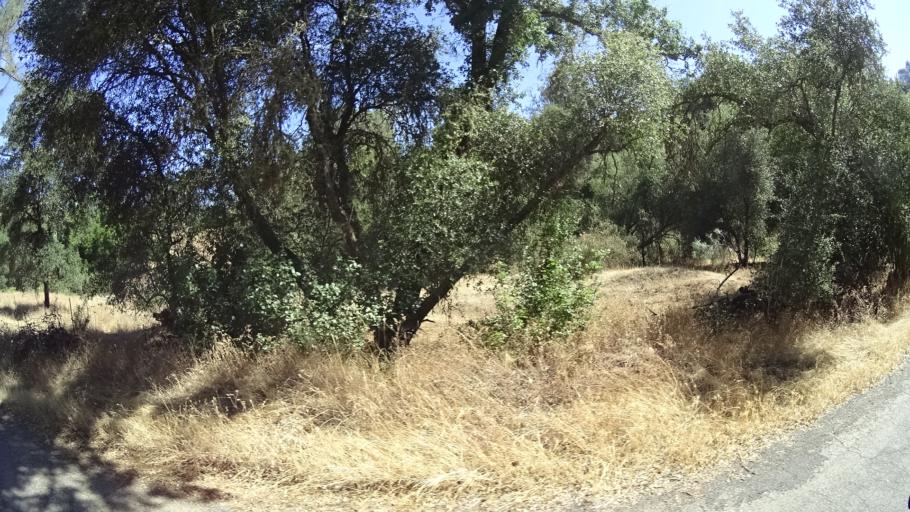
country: US
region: California
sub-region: Calaveras County
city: Angels Camp
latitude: 38.1465
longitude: -120.5705
